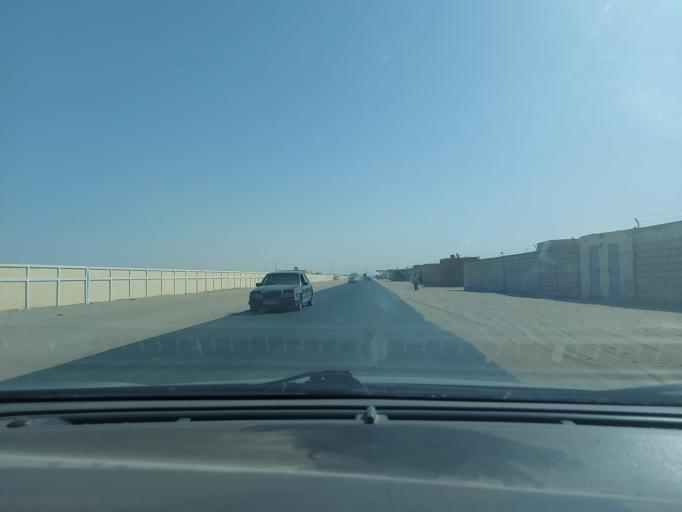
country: MR
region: Nouakchott
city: Nouakchott
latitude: 18.1400
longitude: -15.9194
